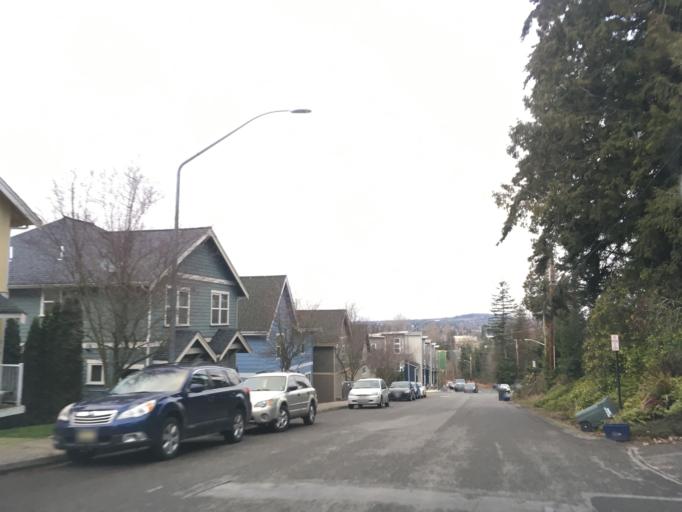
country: US
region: Washington
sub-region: Whatcom County
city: Bellingham
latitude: 48.7327
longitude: -122.4638
